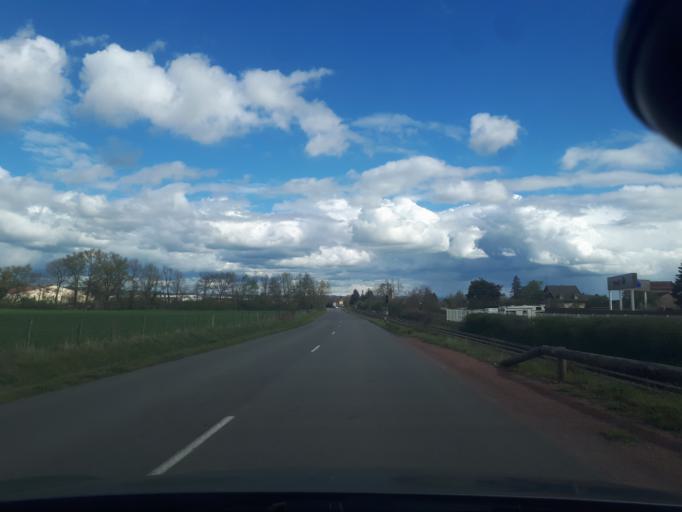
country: FR
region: Rhone-Alpes
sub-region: Departement de la Loire
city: Balbigny
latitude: 45.8252
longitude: 4.1778
